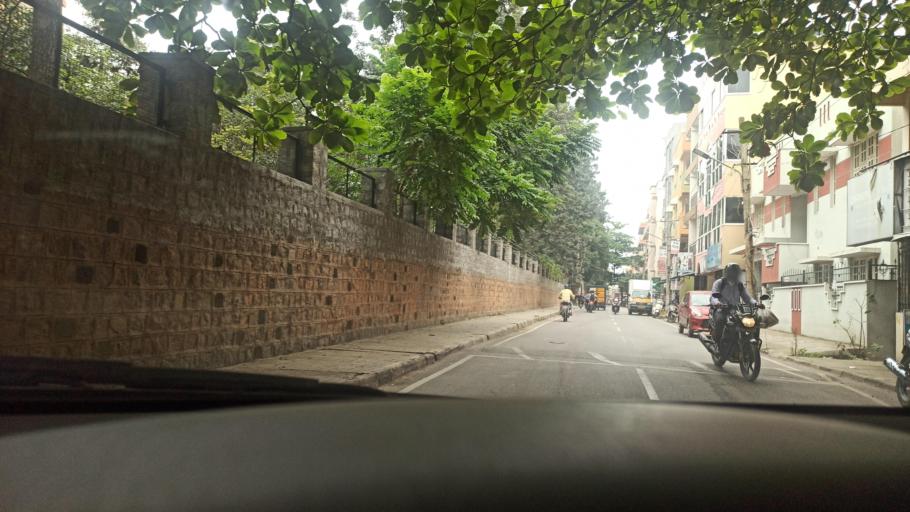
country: IN
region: Karnataka
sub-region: Bangalore Urban
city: Bangalore
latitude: 12.9887
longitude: 77.6795
